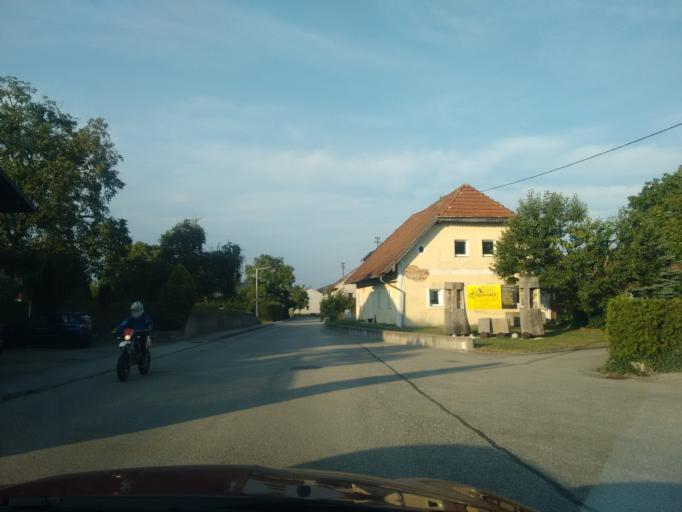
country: AT
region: Upper Austria
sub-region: Politischer Bezirk Vocklabruck
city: Niederthalheim
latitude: 48.1423
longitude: 13.7399
